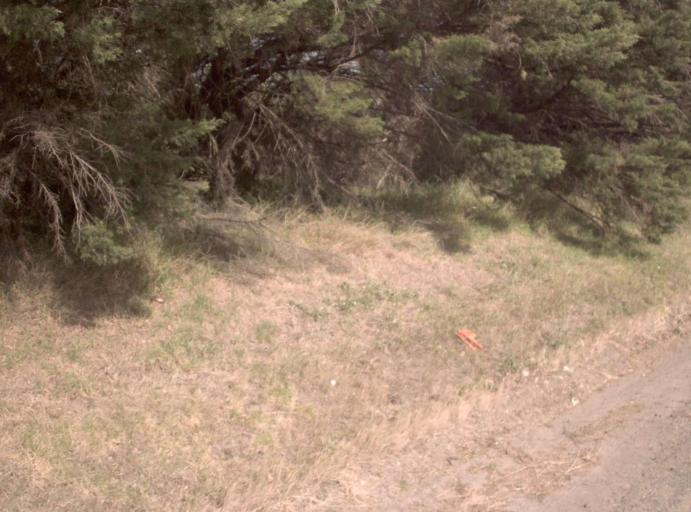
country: AU
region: Victoria
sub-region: Casey
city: Cranbourne East
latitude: -38.1246
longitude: 145.3260
